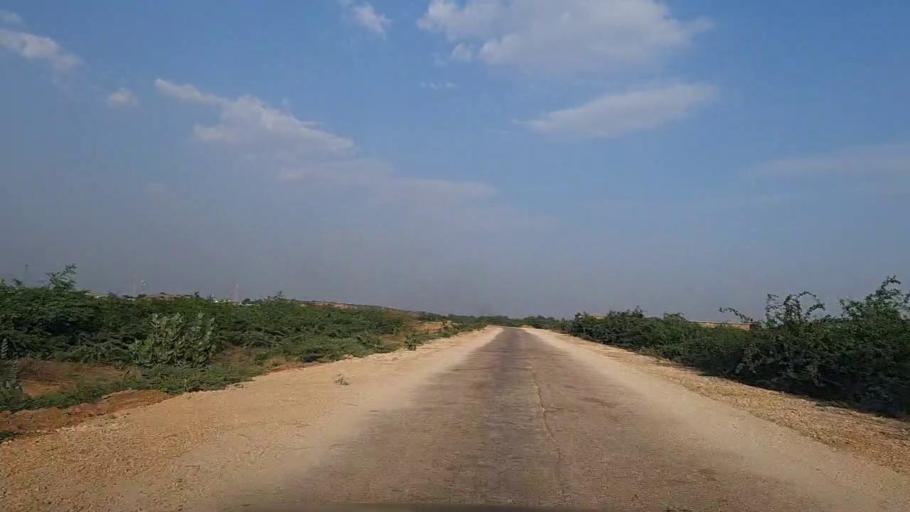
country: PK
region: Sindh
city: Thatta
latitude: 24.8480
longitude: 67.7667
